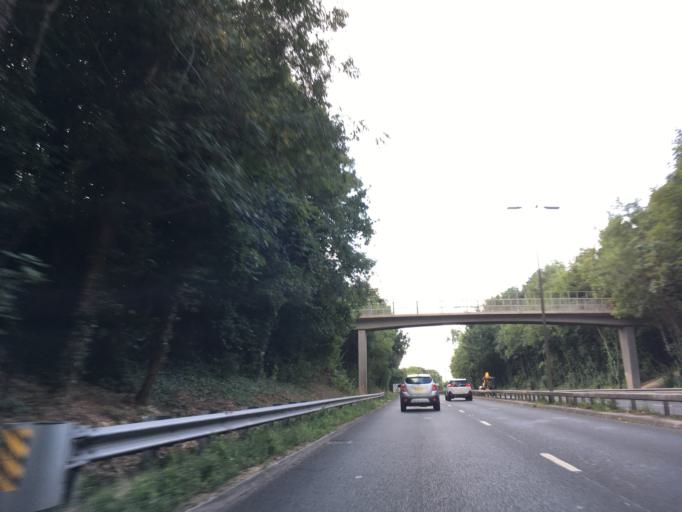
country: GB
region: England
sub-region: West Berkshire
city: Greenham
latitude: 51.3882
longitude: -1.3200
